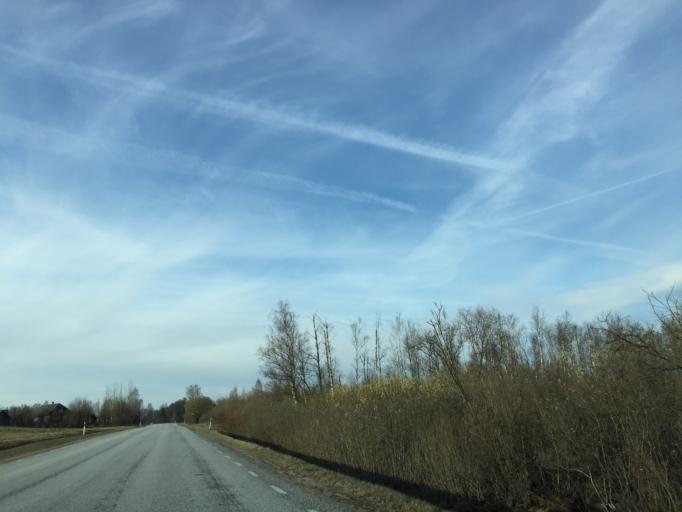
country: EE
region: Tartu
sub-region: Noo vald
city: Noo
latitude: 58.1752
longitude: 26.5503
